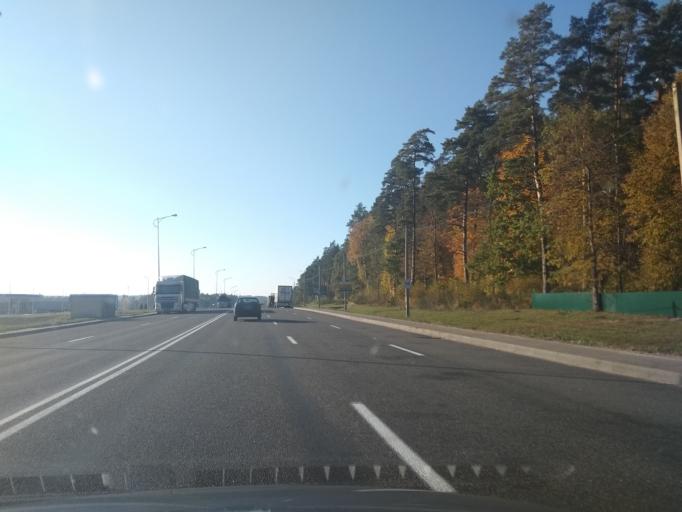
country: BY
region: Grodnenskaya
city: Vyalikaya Byerastavitsa
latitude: 53.1209
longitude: 23.9142
